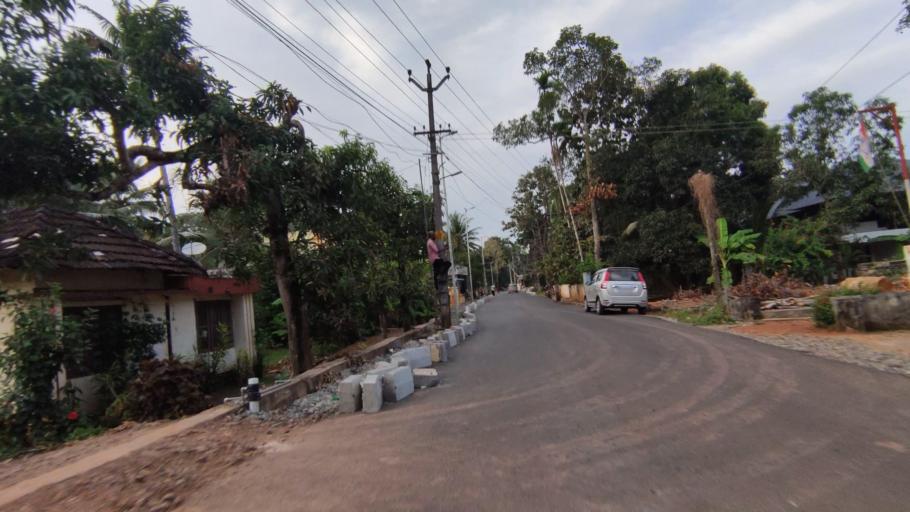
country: IN
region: Kerala
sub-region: Kottayam
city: Kottayam
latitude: 9.6362
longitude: 76.4962
